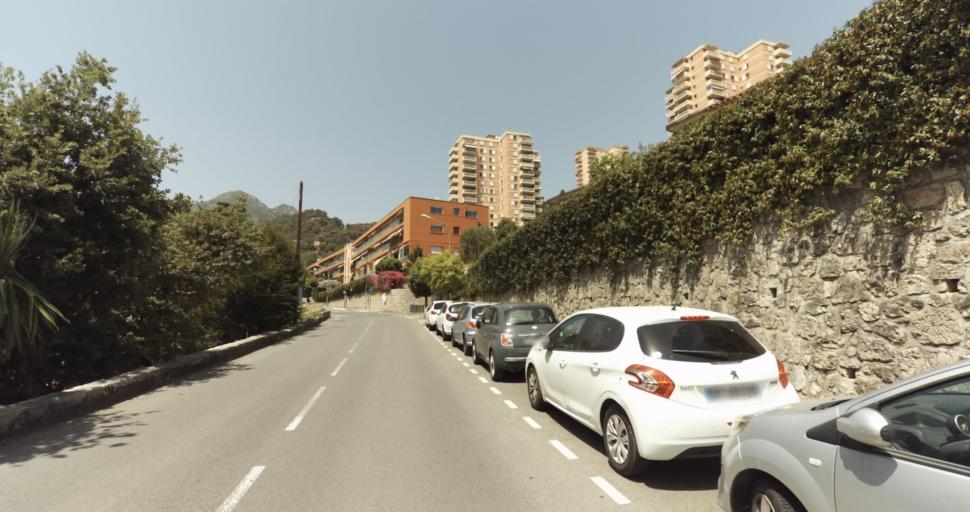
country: FR
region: Provence-Alpes-Cote d'Azur
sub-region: Departement des Alpes-Maritimes
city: Roquebrune-Cap-Martin
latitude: 43.7760
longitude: 7.4737
